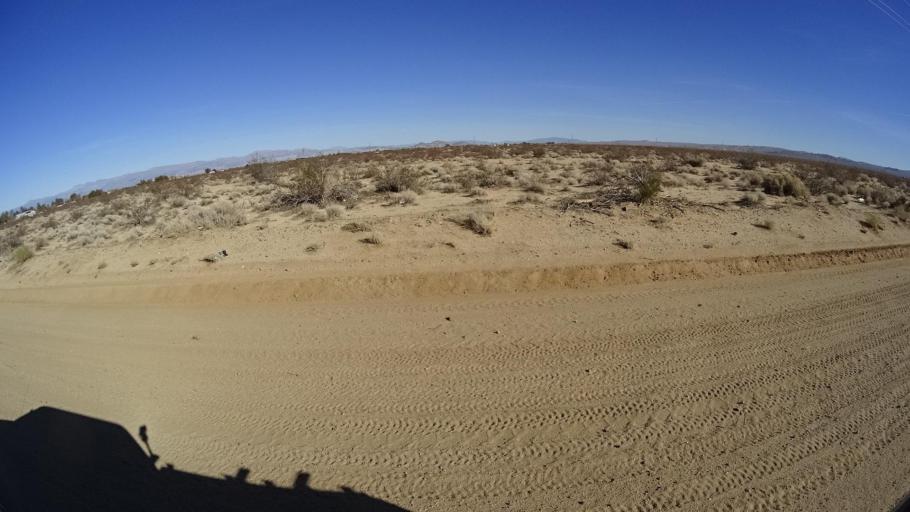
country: US
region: California
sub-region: Kern County
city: Inyokern
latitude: 35.6218
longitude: -117.8048
